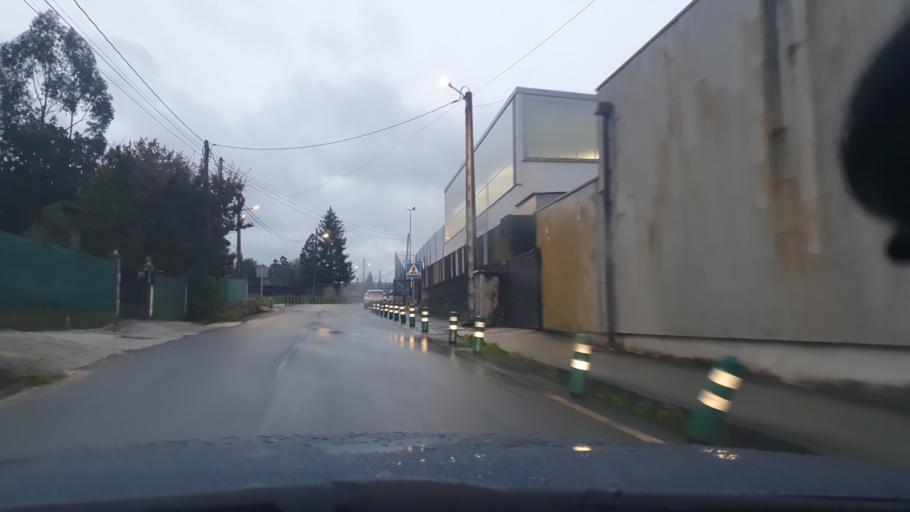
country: ES
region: Galicia
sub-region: Provincia da Coruna
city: Santiago de Compostela
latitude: 42.8516
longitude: -8.5889
